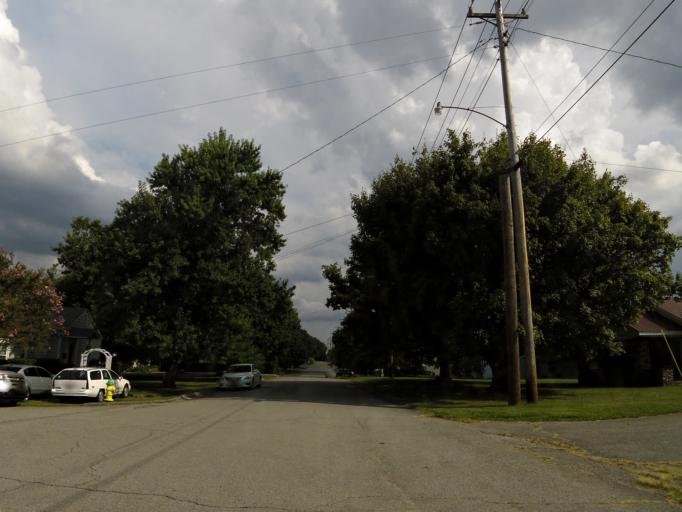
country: US
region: Tennessee
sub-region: Dickson County
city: Dickson
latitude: 36.0828
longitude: -87.3962
